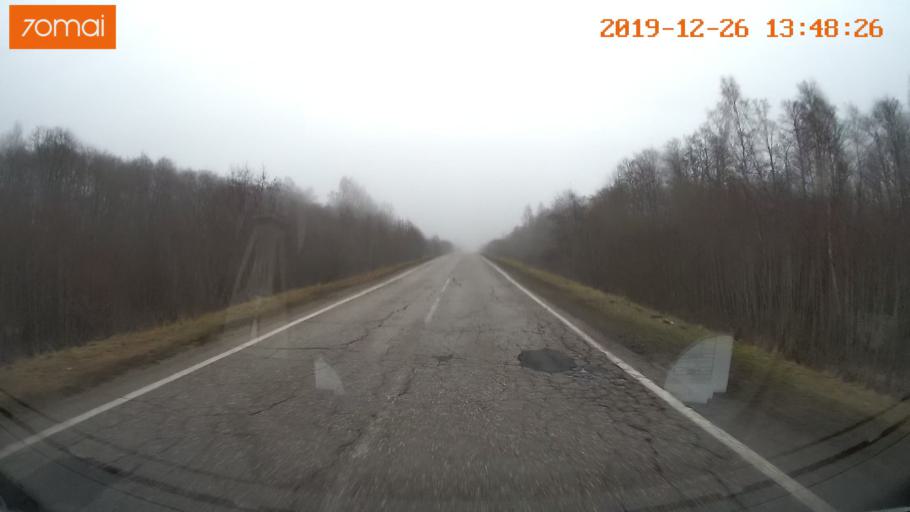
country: RU
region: Vologda
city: Sheksna
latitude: 58.6758
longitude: 38.5484
